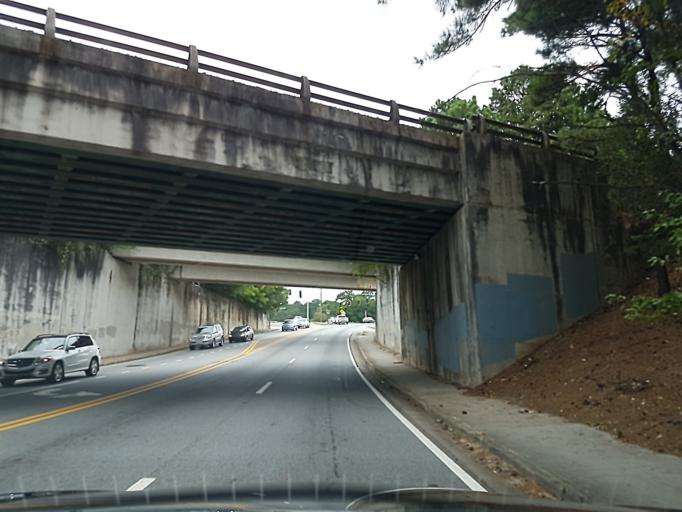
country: US
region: Georgia
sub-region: DeKalb County
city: North Atlanta
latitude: 33.8576
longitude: -84.3403
